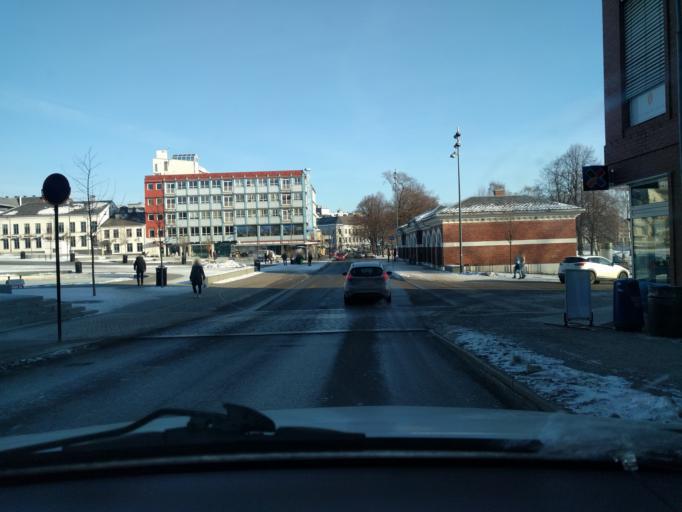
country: NO
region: Hedmark
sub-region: Hamar
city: Hamar
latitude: 60.7945
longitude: 11.0668
